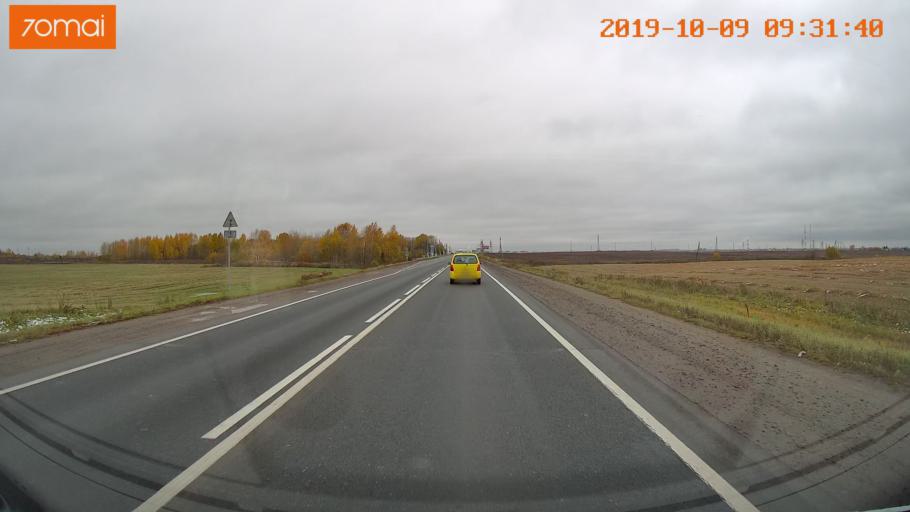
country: RU
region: Vologda
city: Vologda
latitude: 59.1515
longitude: 39.9365
